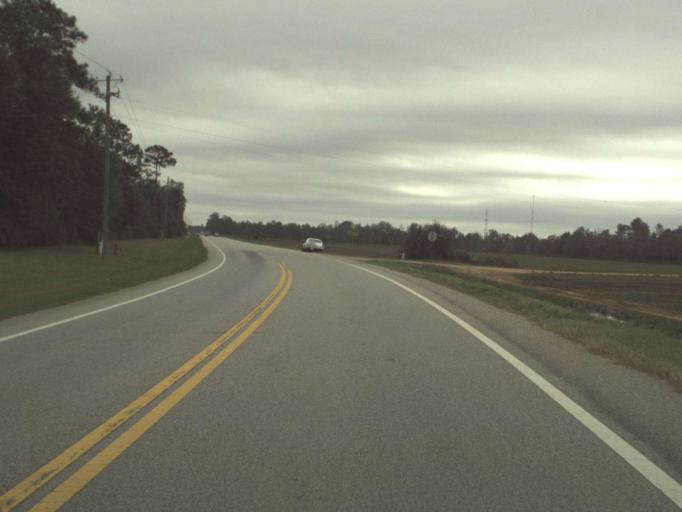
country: US
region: Florida
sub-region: Escambia County
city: Molino
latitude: 30.7503
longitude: -87.3749
